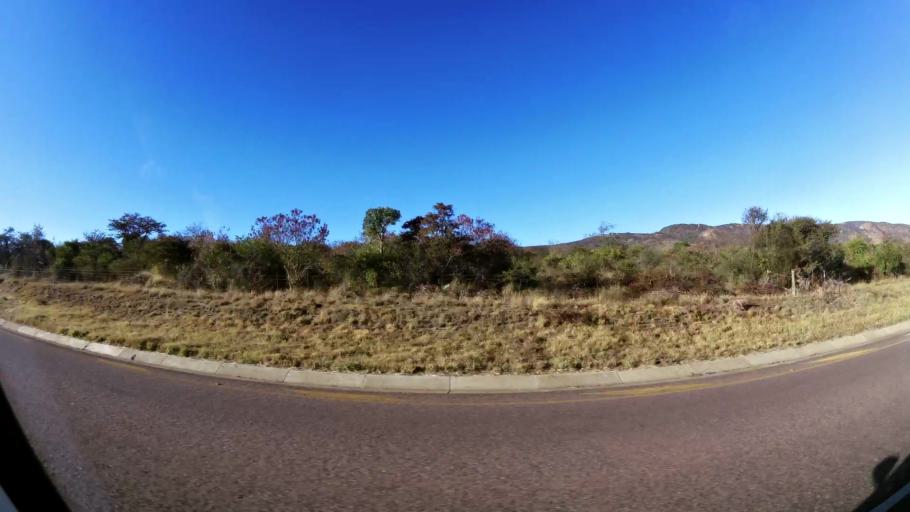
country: ZA
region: Limpopo
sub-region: Capricorn District Municipality
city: Mankoeng
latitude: -23.9198
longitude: 29.8805
